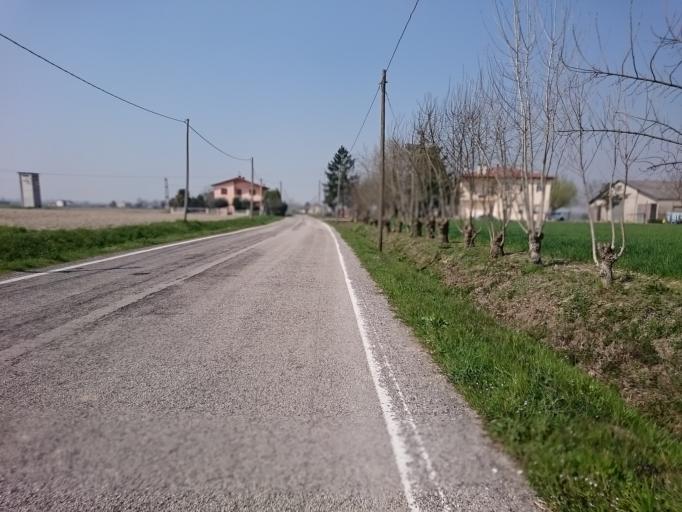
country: IT
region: Veneto
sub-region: Provincia di Padova
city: Villa Estense
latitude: 45.1970
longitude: 11.6669
